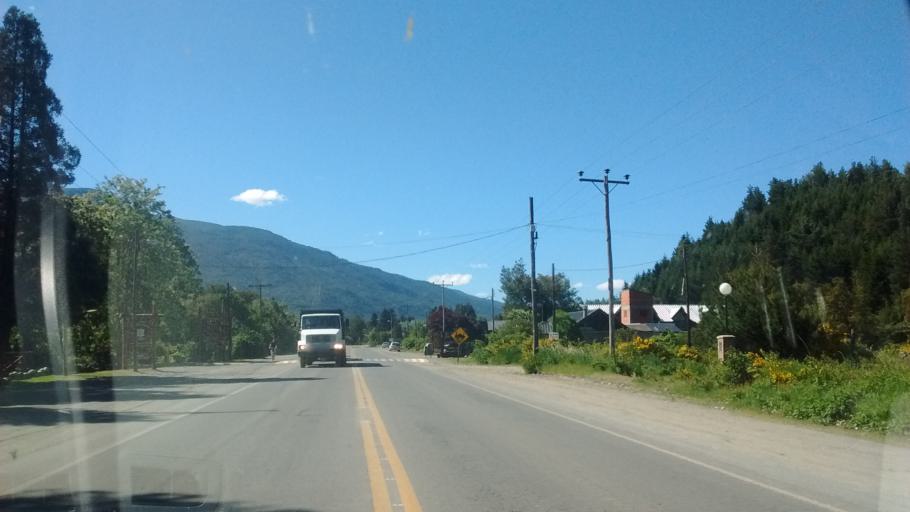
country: AR
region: Chubut
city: Lago Puelo
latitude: -42.0561
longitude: -71.5964
